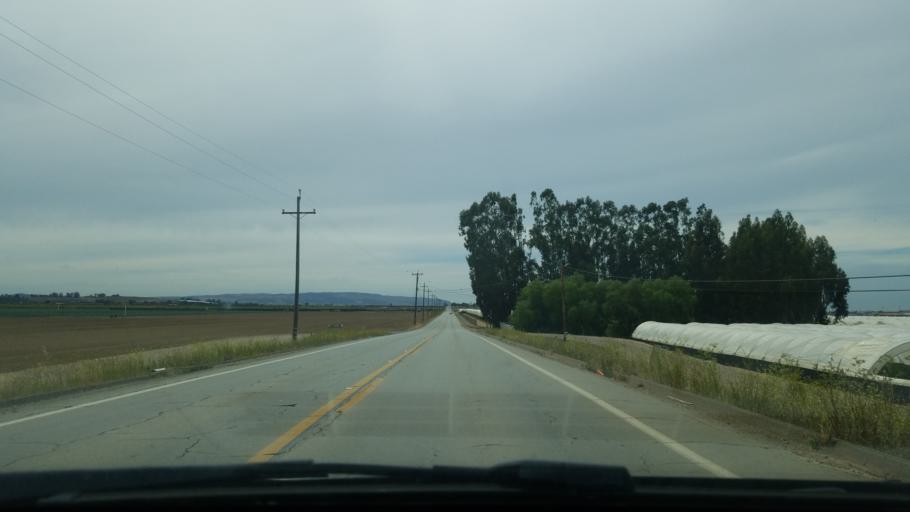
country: US
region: California
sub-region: Santa Barbara County
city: Santa Maria
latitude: 34.9233
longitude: -120.3576
